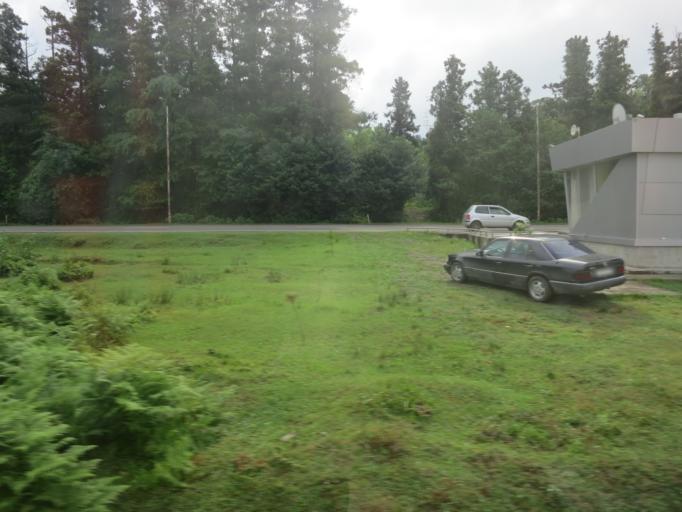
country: GE
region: Guria
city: Urek'i
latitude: 41.9946
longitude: 41.7805
